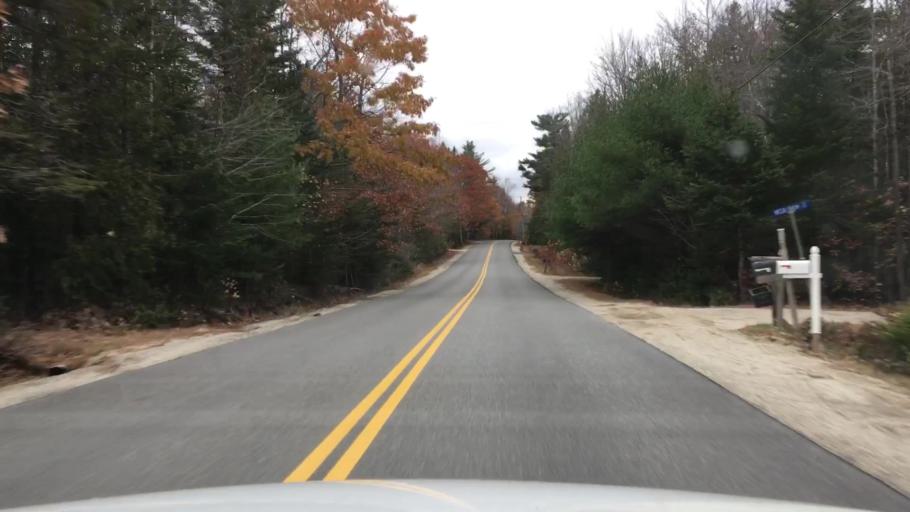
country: US
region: Maine
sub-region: Hancock County
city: Penobscot
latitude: 44.4562
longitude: -68.6376
